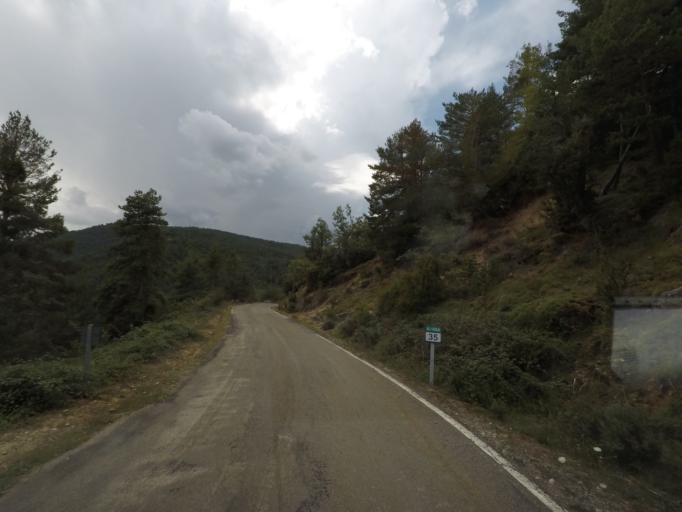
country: ES
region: Aragon
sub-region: Provincia de Huesca
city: Boltana
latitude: 42.3977
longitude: -0.0407
